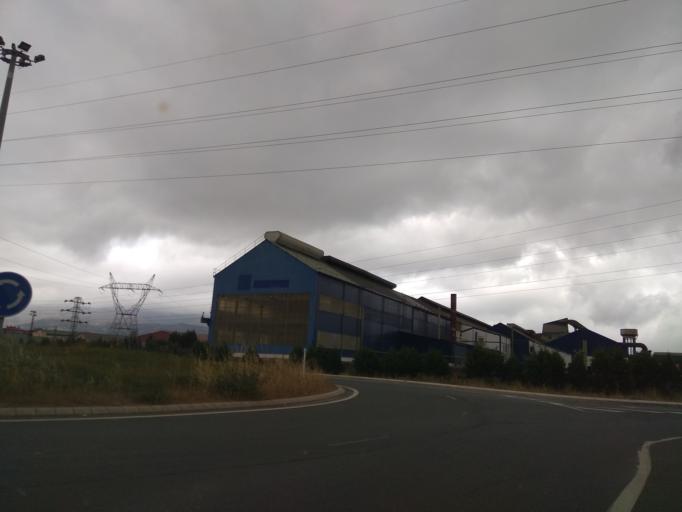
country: ES
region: Cantabria
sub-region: Provincia de Cantabria
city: Reinosa
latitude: 42.9858
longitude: -4.1384
